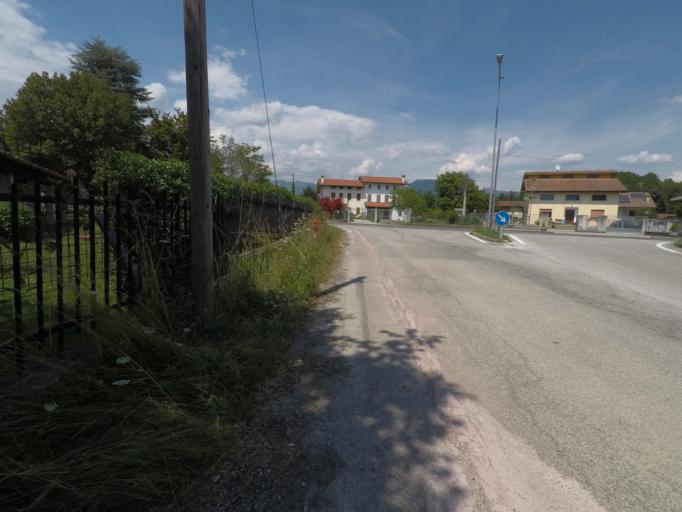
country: IT
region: Friuli Venezia Giulia
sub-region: Provincia di Pordenone
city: Lestans
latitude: 46.1639
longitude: 12.8987
